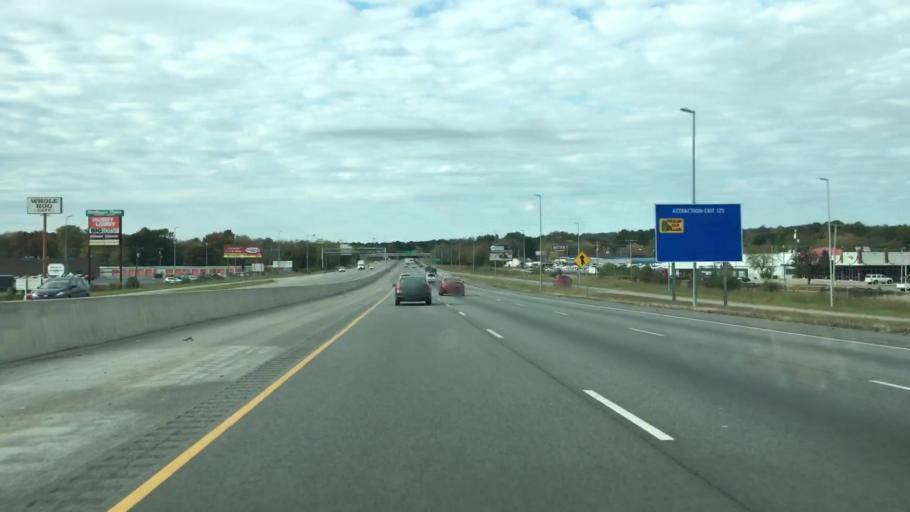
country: US
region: Arkansas
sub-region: Faulkner County
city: Conway
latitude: 35.0934
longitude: -92.4240
